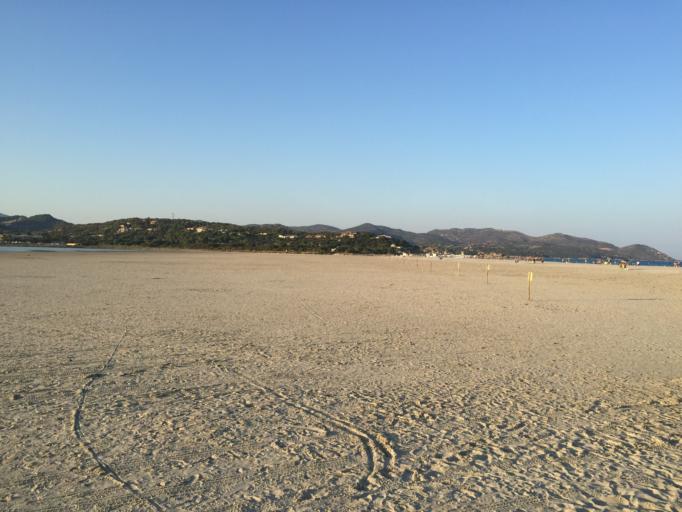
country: IT
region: Sardinia
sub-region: Provincia di Cagliari
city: Villasimius
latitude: 39.1143
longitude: 9.5174
